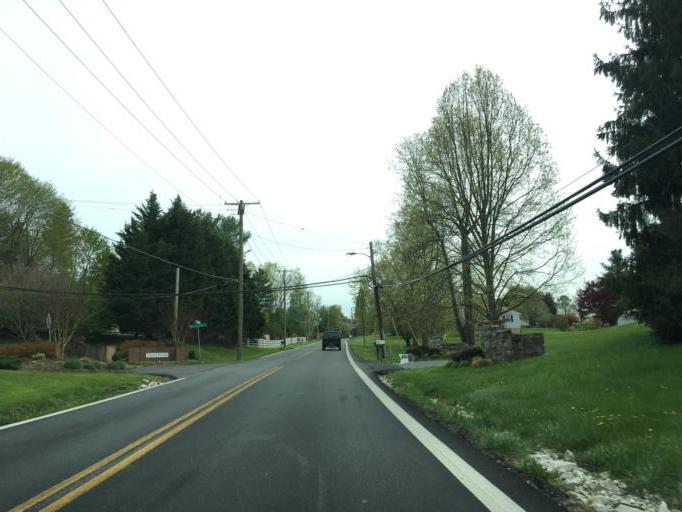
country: US
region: Maryland
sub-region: Baltimore County
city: Hampton
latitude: 39.4934
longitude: -76.5672
